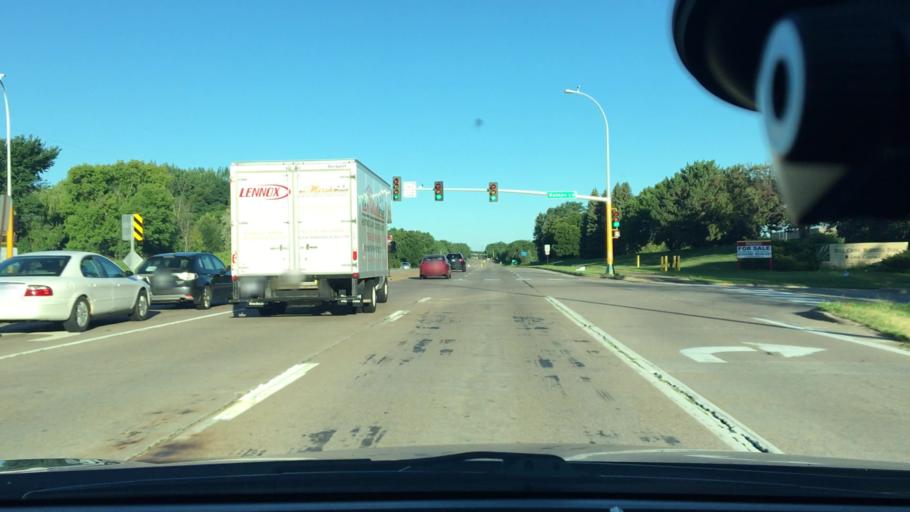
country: US
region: Minnesota
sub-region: Hennepin County
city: New Hope
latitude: 45.0585
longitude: -93.4079
